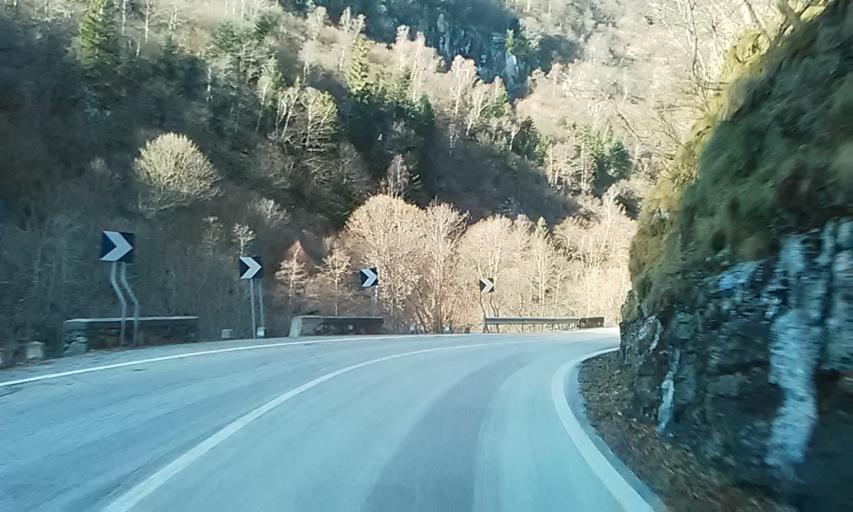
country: IT
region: Piedmont
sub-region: Provincia di Vercelli
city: Rimasco
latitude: 45.8443
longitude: 8.0681
